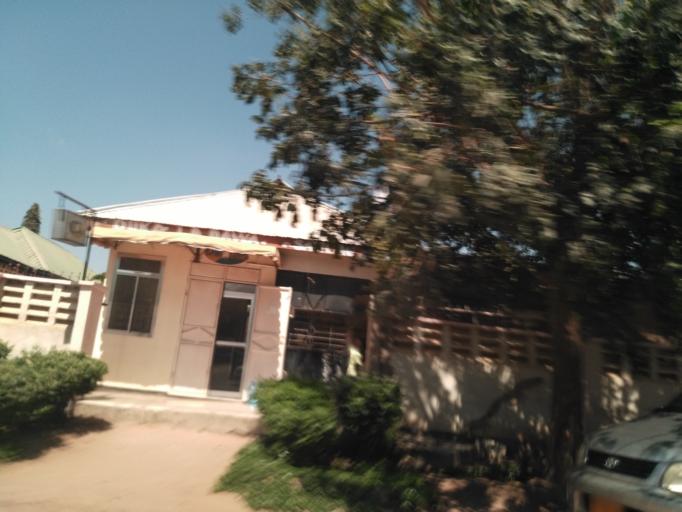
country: TZ
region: Dodoma
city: Dodoma
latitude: -6.1649
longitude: 35.7561
